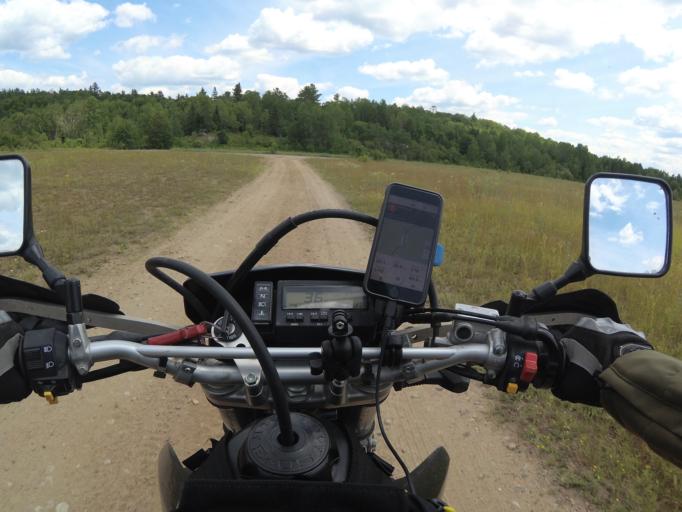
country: CA
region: Ontario
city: Bancroft
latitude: 45.0325
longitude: -77.2657
